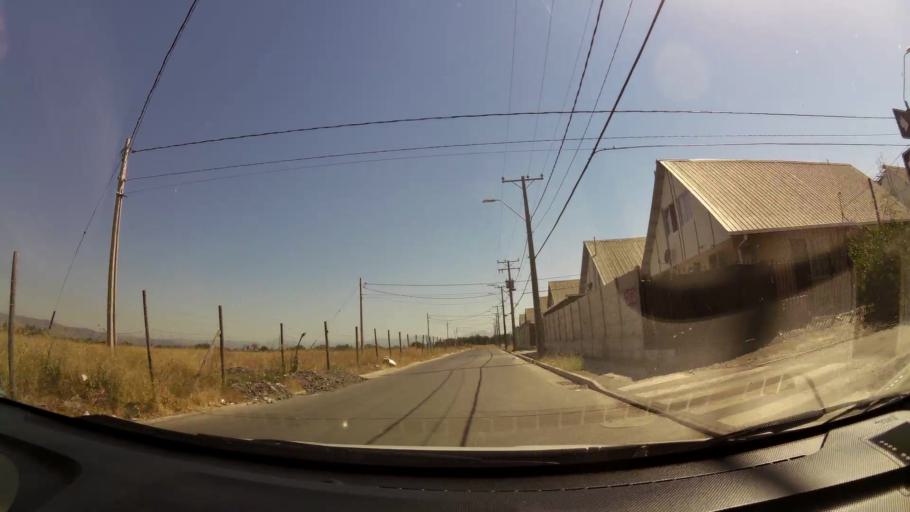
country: CL
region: Maule
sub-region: Provincia de Curico
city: Curico
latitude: -34.9629
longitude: -71.2373
